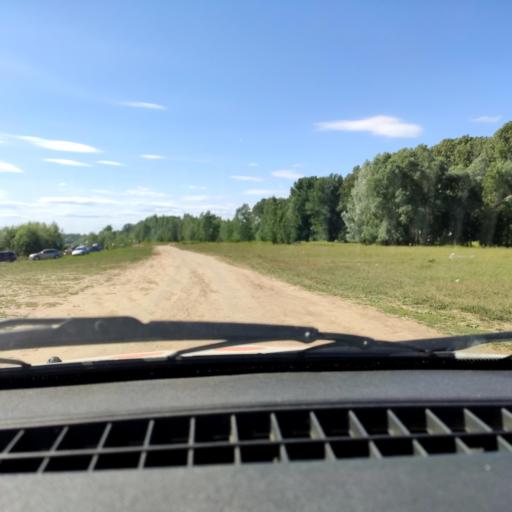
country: RU
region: Bashkortostan
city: Iglino
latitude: 54.7989
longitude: 56.2284
